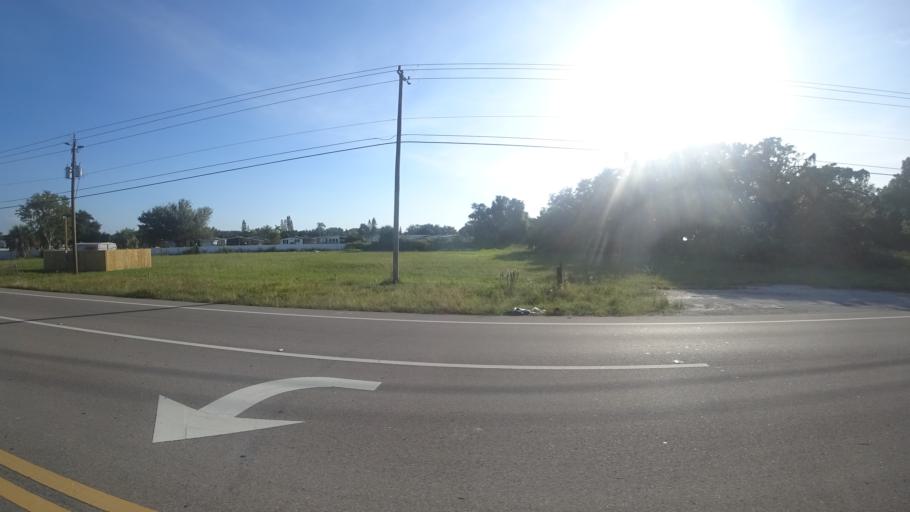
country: US
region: Florida
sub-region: Manatee County
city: West Samoset
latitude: 27.4592
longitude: -82.5531
